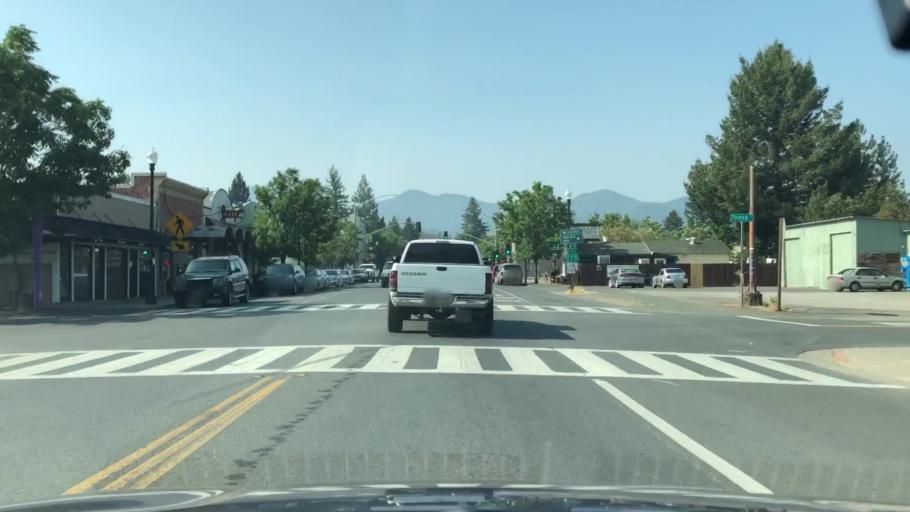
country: US
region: California
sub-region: Lake County
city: Middletown
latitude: 38.7533
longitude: -122.6149
